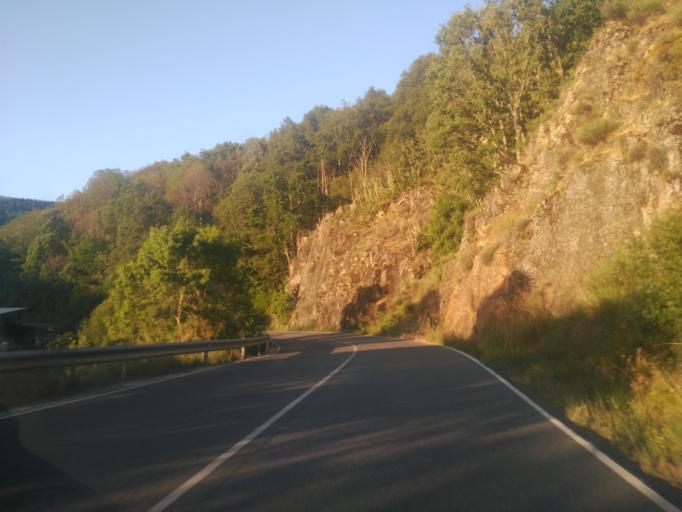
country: ES
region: Castille and Leon
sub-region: Provincia de Salamanca
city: Candelario
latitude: 40.3761
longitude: -5.7505
